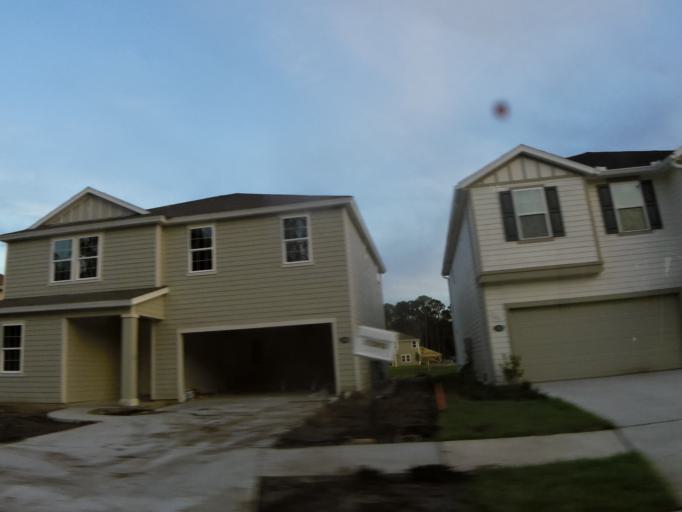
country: US
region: Florida
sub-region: Saint Johns County
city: Fruit Cove
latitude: 30.1510
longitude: -81.5191
